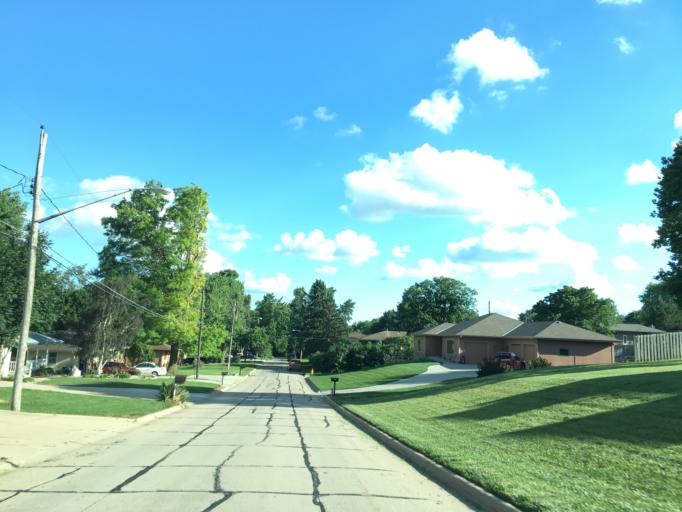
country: US
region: Nebraska
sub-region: Sarpy County
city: La Vista
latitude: 41.1898
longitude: -95.9819
